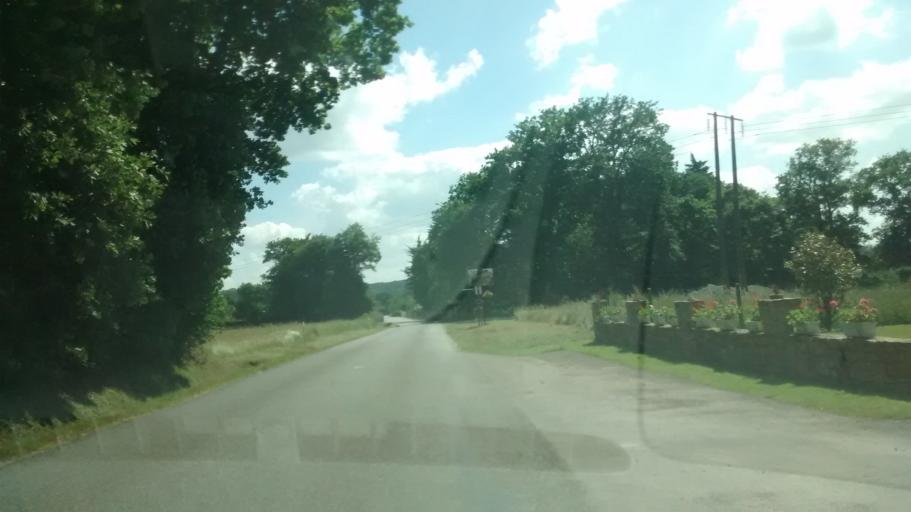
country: FR
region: Brittany
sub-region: Departement du Morbihan
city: Malestroit
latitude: 47.8189
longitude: -2.3725
